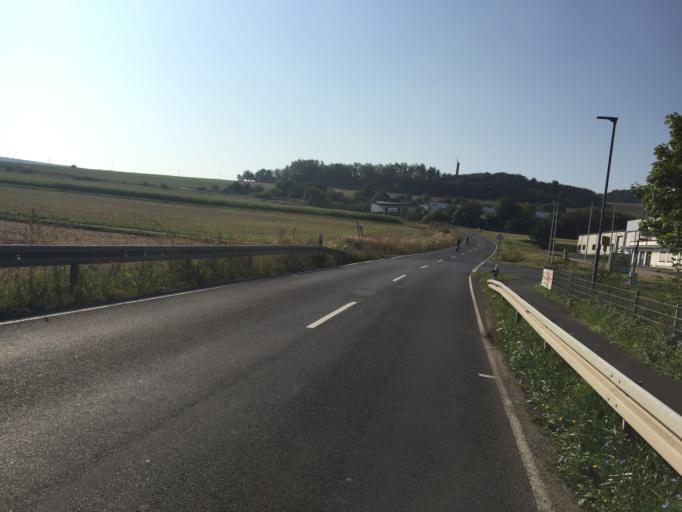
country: DE
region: Hesse
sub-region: Regierungsbezirk Giessen
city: Hoernsheim
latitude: 50.4601
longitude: 8.5962
